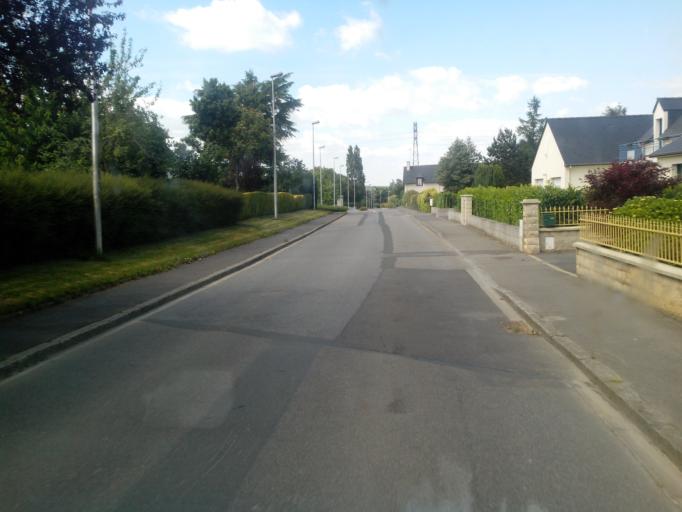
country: FR
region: Brittany
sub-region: Departement d'Ille-et-Vilaine
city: Acigne
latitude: 48.1385
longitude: -1.5325
